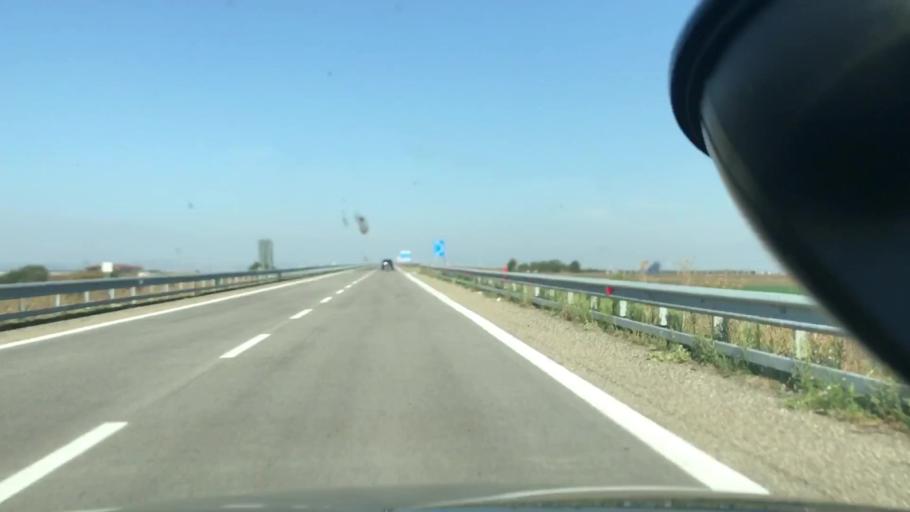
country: IT
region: Basilicate
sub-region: Provincia di Potenza
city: Montemilone
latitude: 40.9911
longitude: 15.8966
